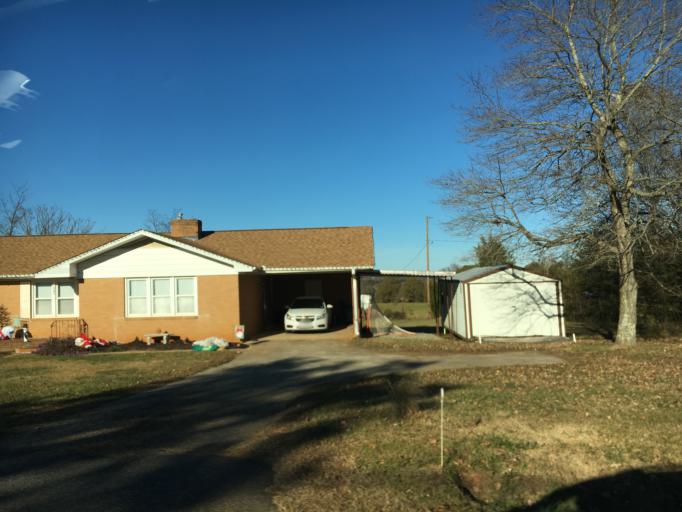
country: US
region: South Carolina
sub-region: Greenville County
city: Greer
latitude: 34.9637
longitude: -82.1888
